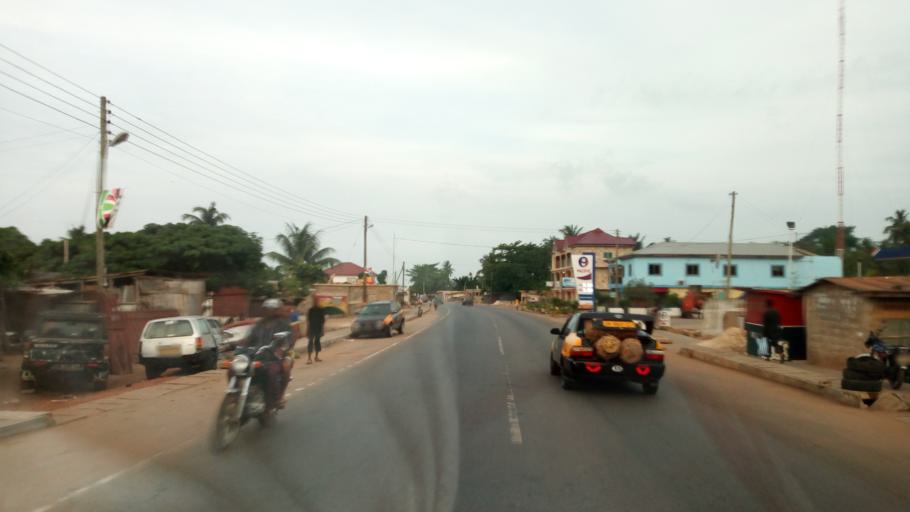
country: TG
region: Maritime
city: Lome
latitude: 6.1215
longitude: 1.1839
